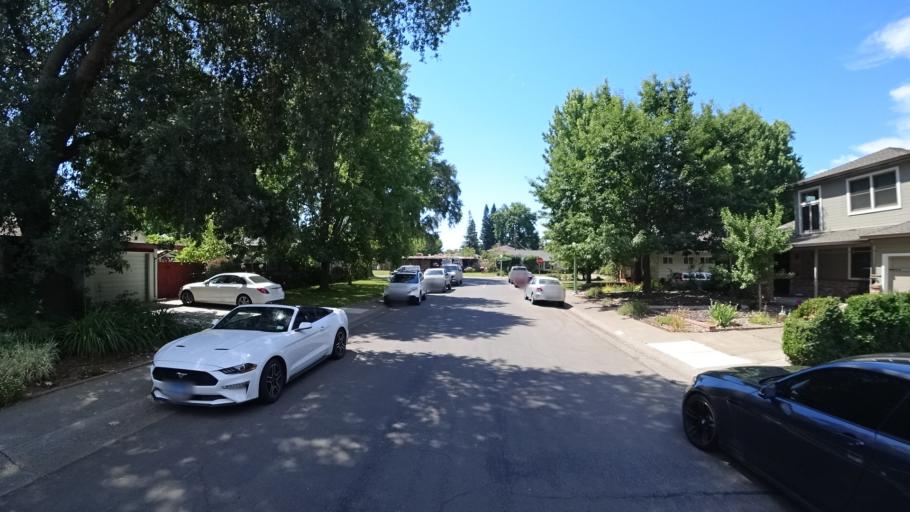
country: US
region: California
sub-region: Sacramento County
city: Arden-Arcade
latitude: 38.5739
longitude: -121.4252
